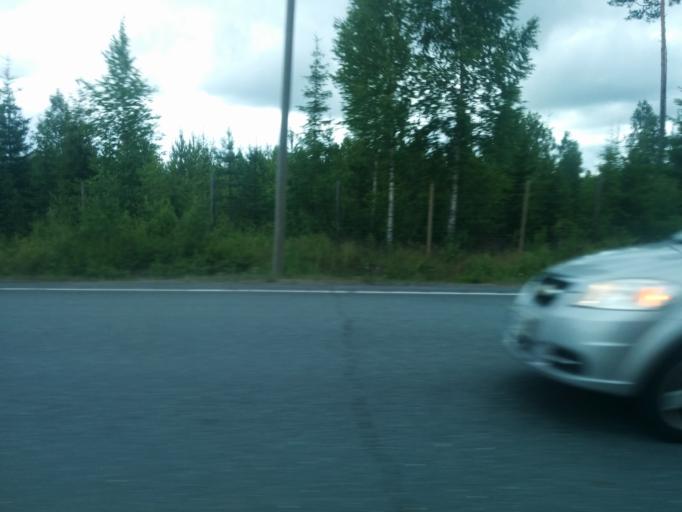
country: FI
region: Pirkanmaa
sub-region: Tampere
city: Orivesi
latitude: 61.6700
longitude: 24.2842
